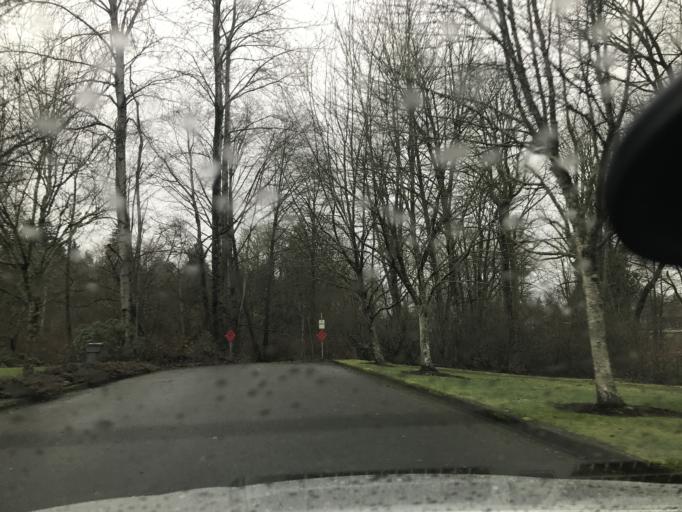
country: US
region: Washington
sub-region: King County
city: Kirkland
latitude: 47.6723
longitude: -122.1910
